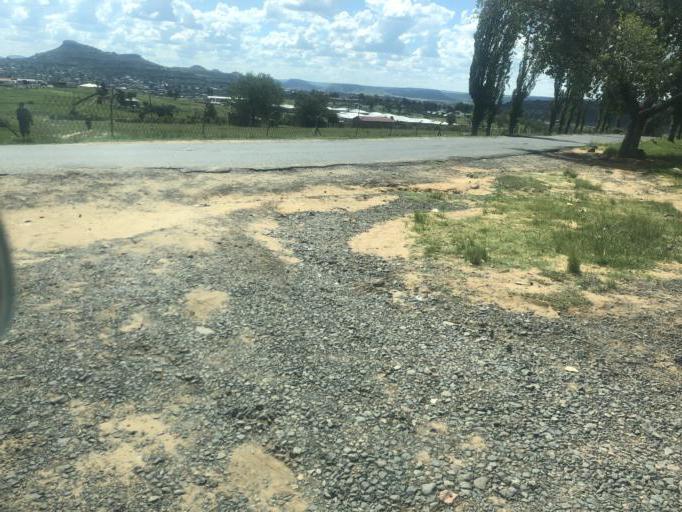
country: LS
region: Maseru
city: Maseru
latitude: -29.3485
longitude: 27.5350
